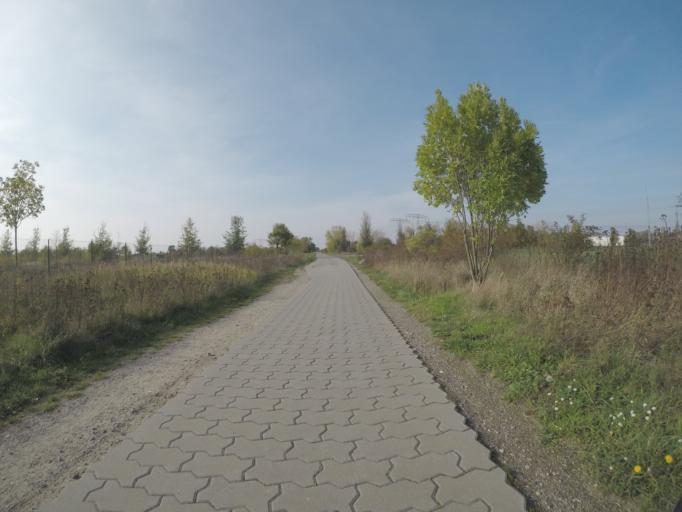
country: DE
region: Brandenburg
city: Schonefeld
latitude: 52.3930
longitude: 13.4884
